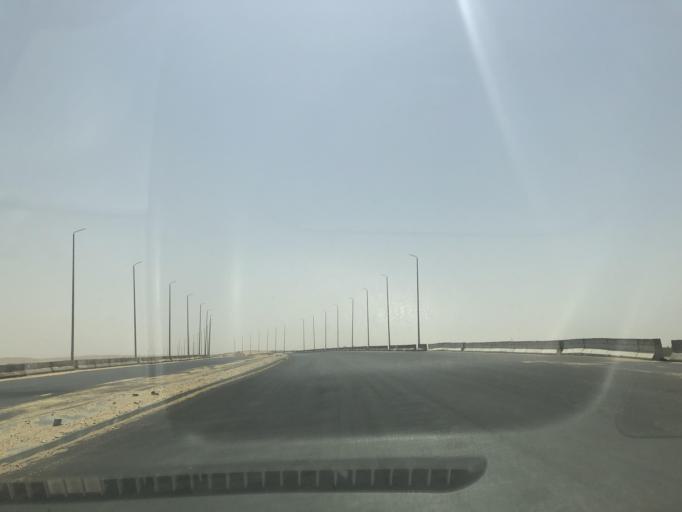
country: EG
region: Al Jizah
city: Madinat Sittah Uktubar
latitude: 29.9179
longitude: 31.0205
